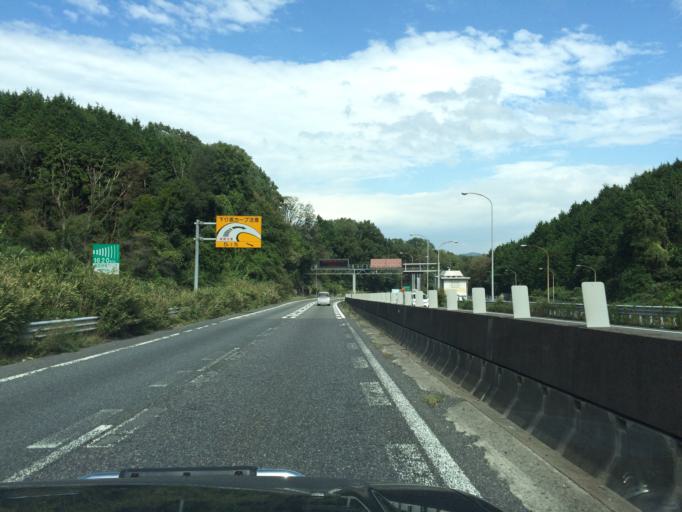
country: JP
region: Mie
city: Nabari
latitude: 34.6876
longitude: 136.0476
